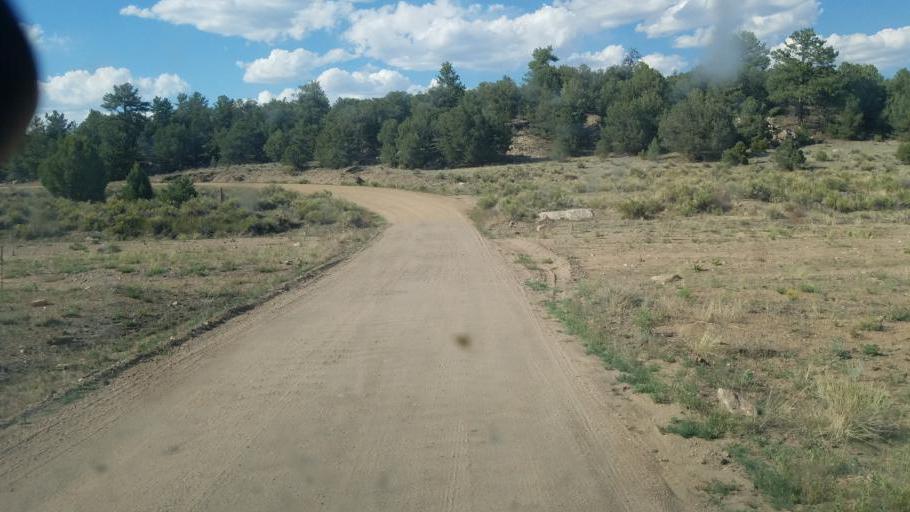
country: US
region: Colorado
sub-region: Custer County
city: Westcliffe
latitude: 38.2805
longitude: -105.4701
